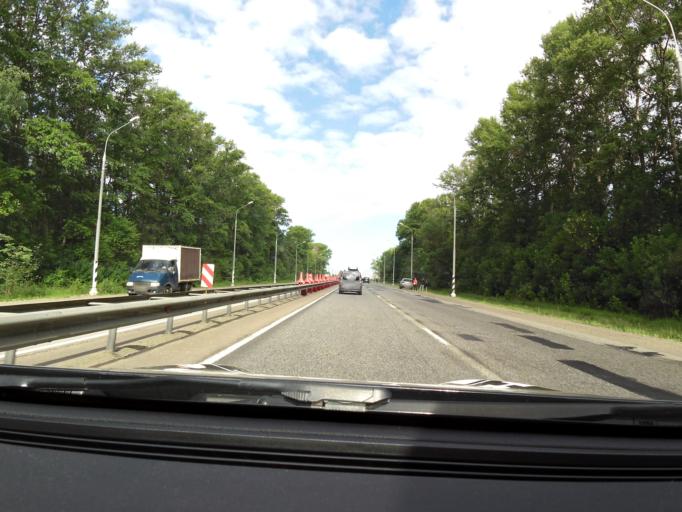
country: RU
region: Tverskaya
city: Gorodnya
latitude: 56.7428
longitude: 36.2341
